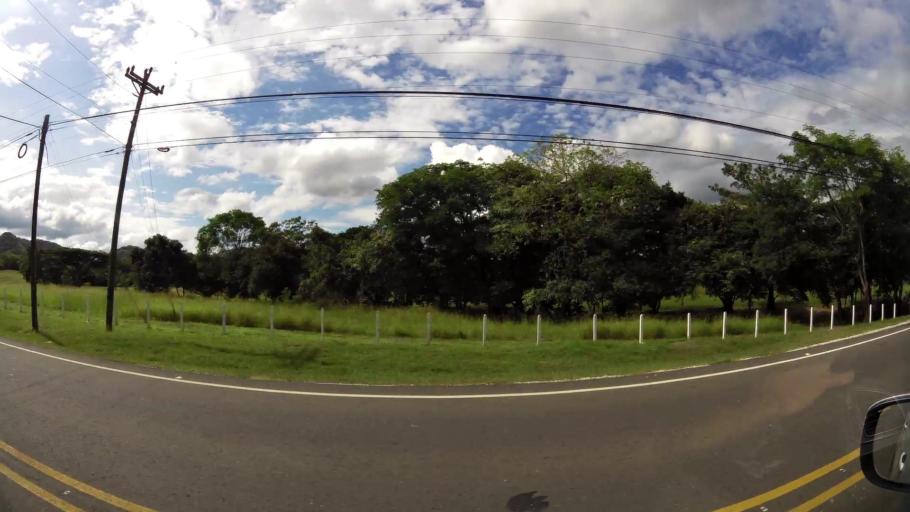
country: CR
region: Guanacaste
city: Hojancha
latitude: 10.1321
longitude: -85.3414
